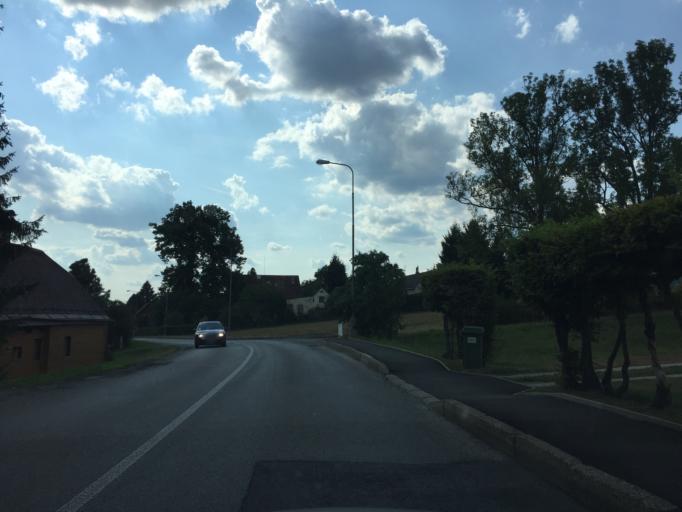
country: CZ
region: Liberecky
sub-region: Okres Jablonec nad Nisou
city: Jablonec nad Nisou
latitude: 50.7008
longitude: 15.1751
